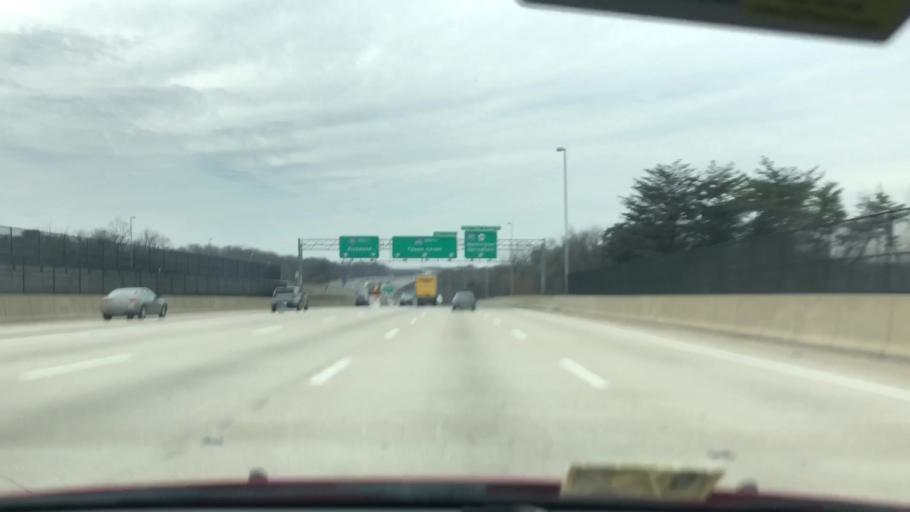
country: US
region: Virginia
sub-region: Fairfax County
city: Franconia
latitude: 38.7946
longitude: -77.1538
